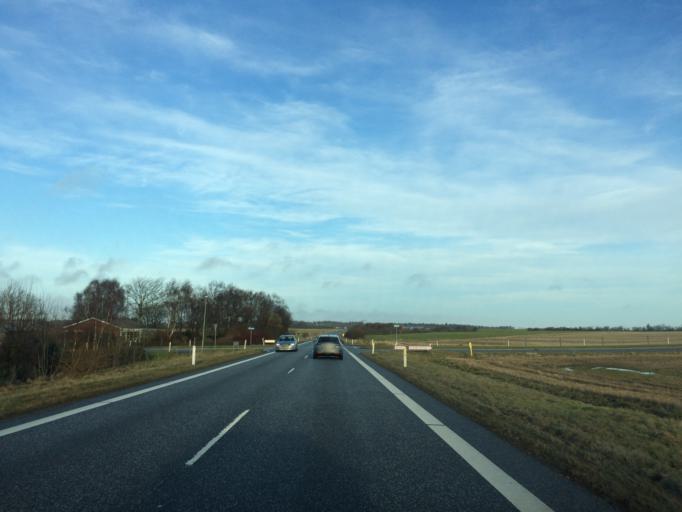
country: DK
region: North Denmark
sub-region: Thisted Kommune
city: Hurup
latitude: 56.8197
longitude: 8.4922
